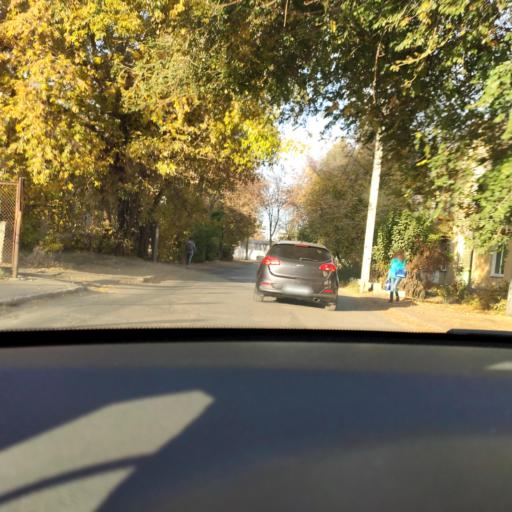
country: RU
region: Samara
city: Samara
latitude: 53.2021
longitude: 50.1798
